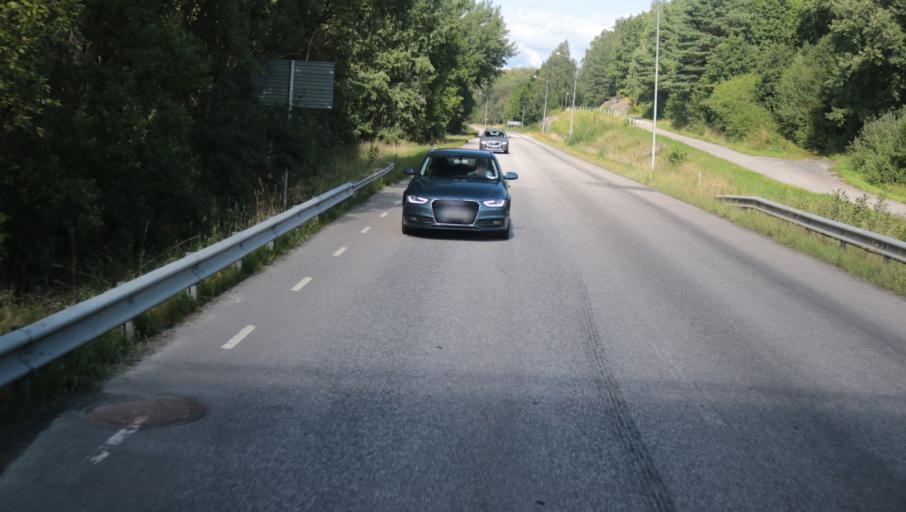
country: SE
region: Blekinge
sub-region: Karlshamns Kommun
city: Karlshamn
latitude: 56.1622
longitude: 14.8525
